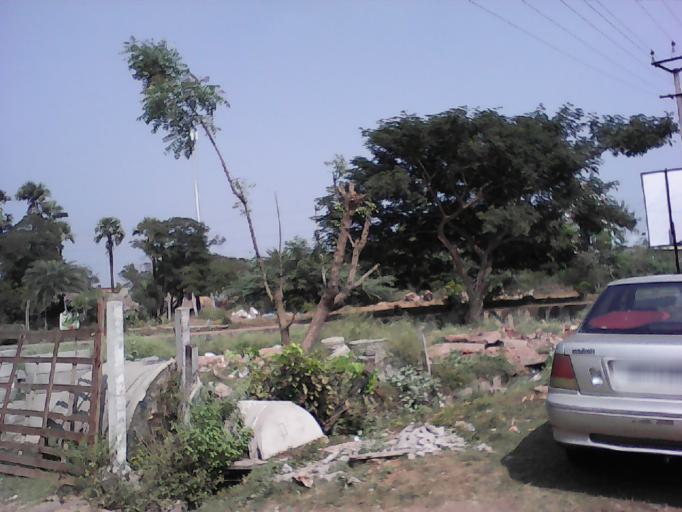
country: IN
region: Andhra Pradesh
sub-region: Guntur
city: Bhattiprolu
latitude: 16.2368
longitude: 80.6594
